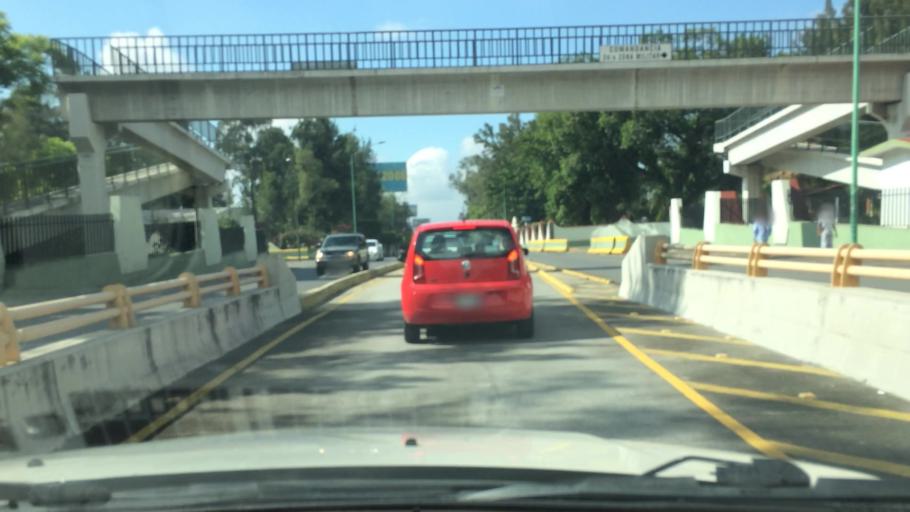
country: MX
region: Morelos
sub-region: Cuernavaca
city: Fraccionamiento Lomas de Ahuatlan
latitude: 18.9638
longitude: -99.2466
